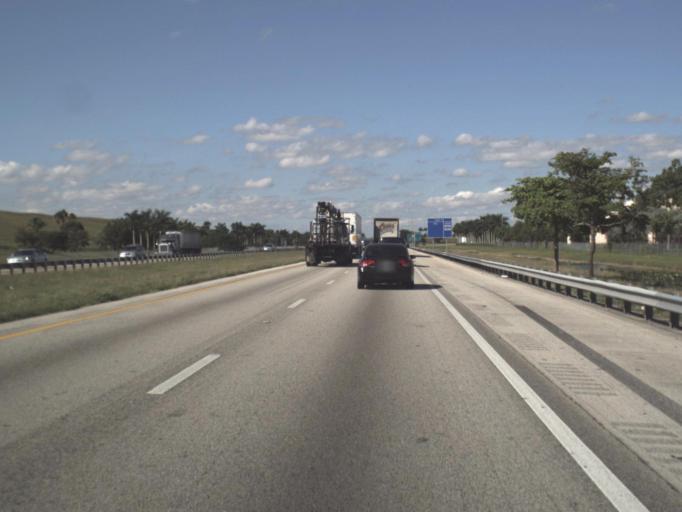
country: US
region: Florida
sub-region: Miami-Dade County
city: Country Club
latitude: 25.9714
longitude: -80.2839
